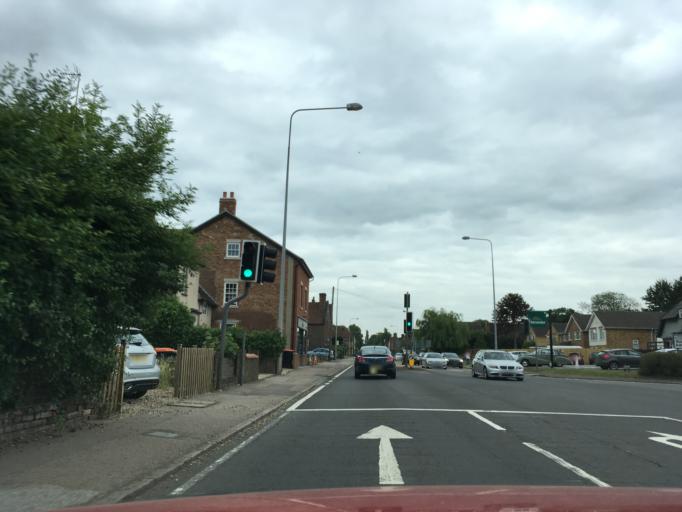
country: GB
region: England
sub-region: Central Bedfordshire
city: Hockliffe
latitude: 51.9312
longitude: -0.5863
